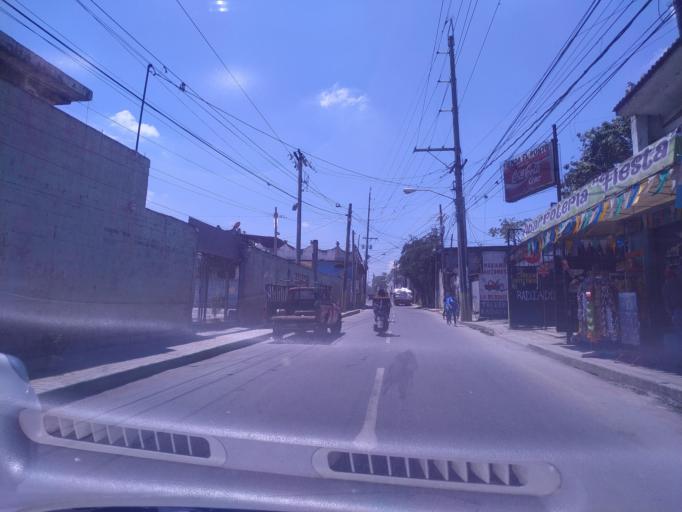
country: GT
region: Guatemala
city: Mixco
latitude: 14.6767
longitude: -90.5721
